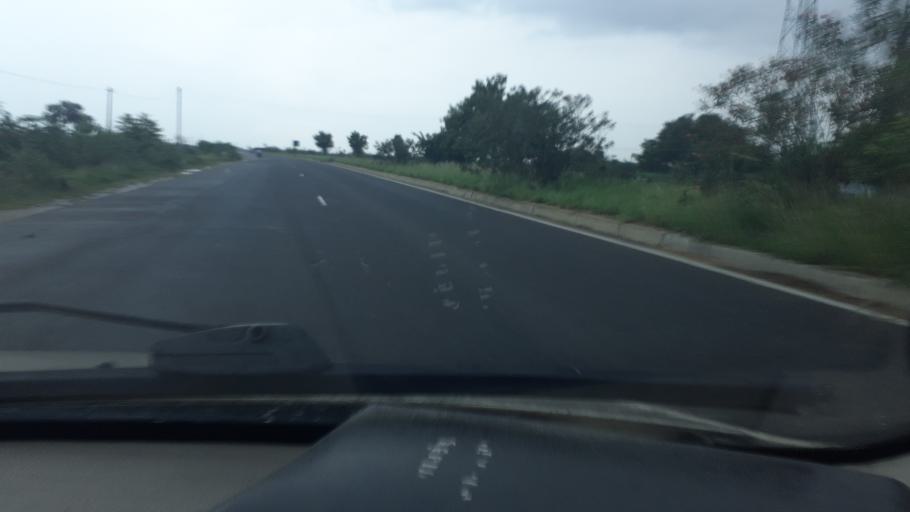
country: IN
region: Tamil Nadu
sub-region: Thoothukkudi
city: Kadambur
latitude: 9.0653
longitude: 77.7986
